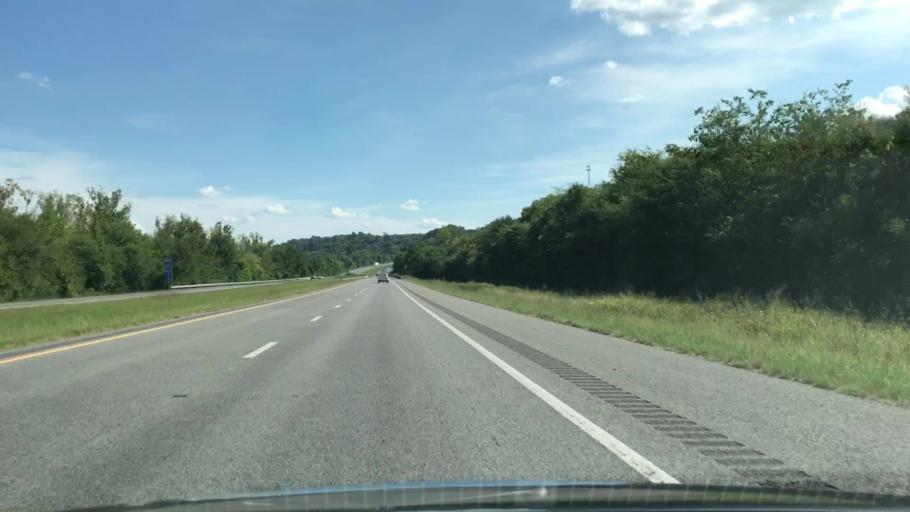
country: US
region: Alabama
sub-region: Limestone County
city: Ardmore
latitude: 35.1338
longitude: -86.8780
